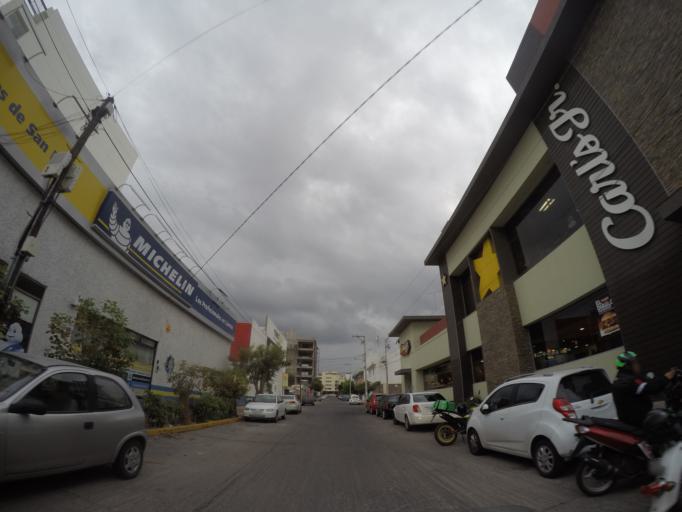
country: MX
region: San Luis Potosi
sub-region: San Luis Potosi
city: San Luis Potosi
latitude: 22.1481
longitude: -101.0172
